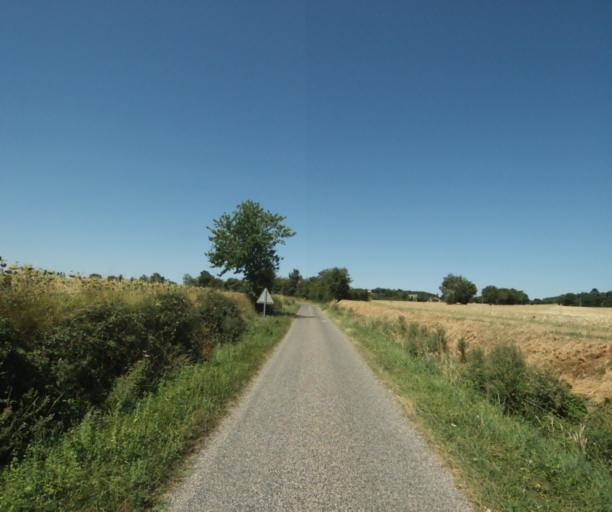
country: FR
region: Midi-Pyrenees
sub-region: Departement de la Haute-Garonne
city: Saint-Felix-Lauragais
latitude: 43.4902
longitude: 1.9431
